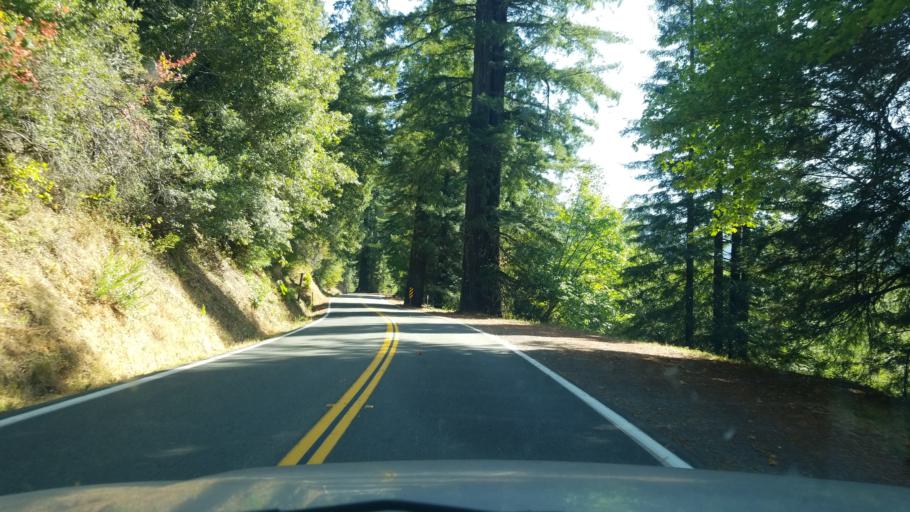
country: US
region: California
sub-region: Humboldt County
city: Redway
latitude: 40.2482
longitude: -123.8230
